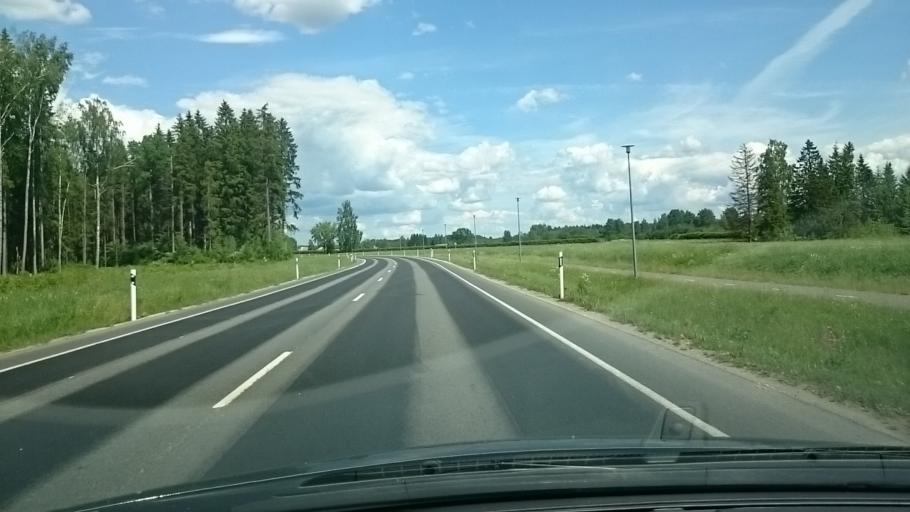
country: EE
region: Jaervamaa
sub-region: Tueri vald
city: Tueri
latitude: 58.8310
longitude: 25.4651
